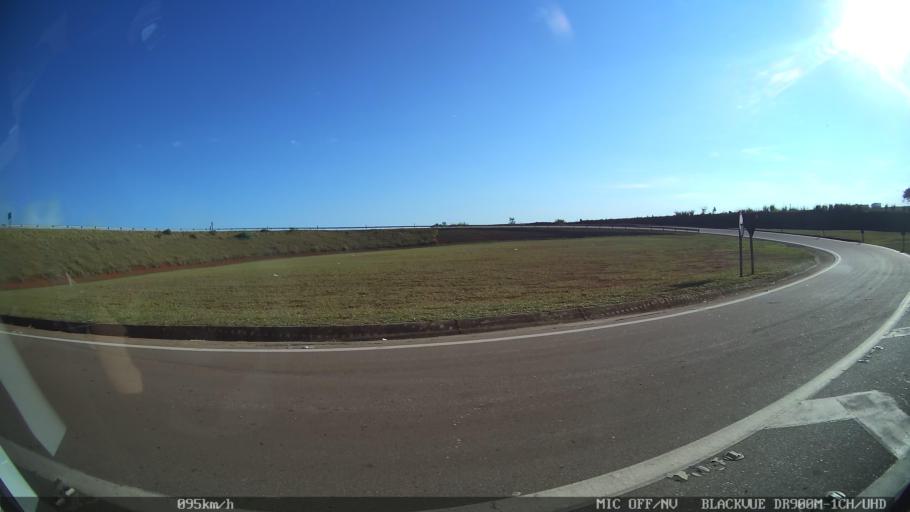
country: BR
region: Sao Paulo
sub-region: Piracicaba
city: Piracicaba
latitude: -22.6793
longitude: -47.5959
